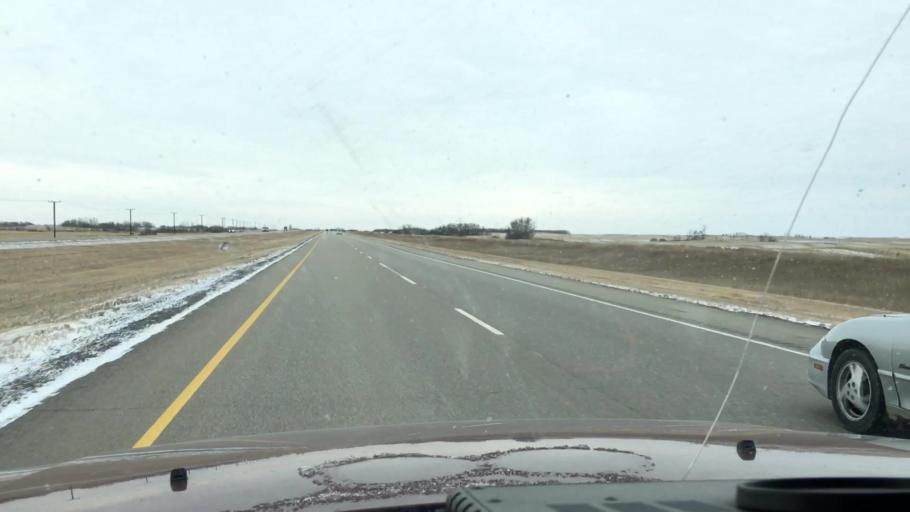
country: CA
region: Saskatchewan
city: Watrous
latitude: 51.3999
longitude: -106.1761
